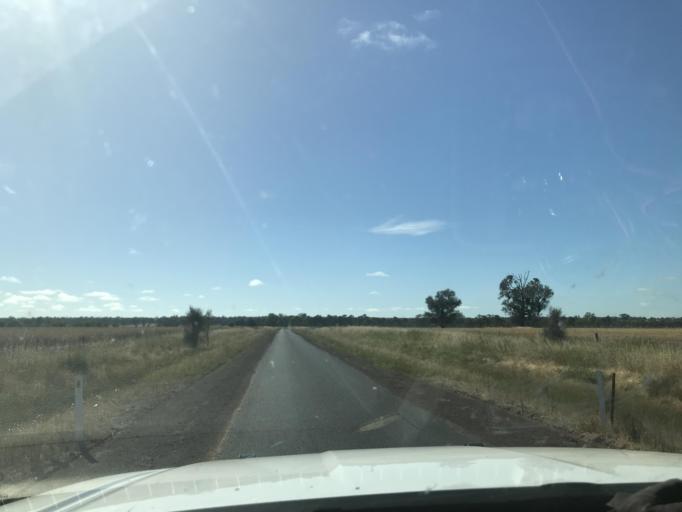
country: AU
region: Victoria
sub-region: Horsham
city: Horsham
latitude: -37.0840
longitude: 141.7494
